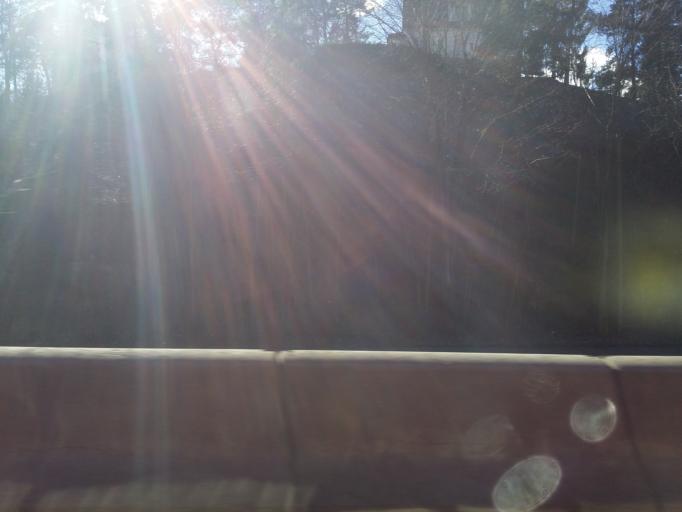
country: NO
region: Oslo
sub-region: Oslo
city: Oslo
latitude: 59.8795
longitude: 10.7747
